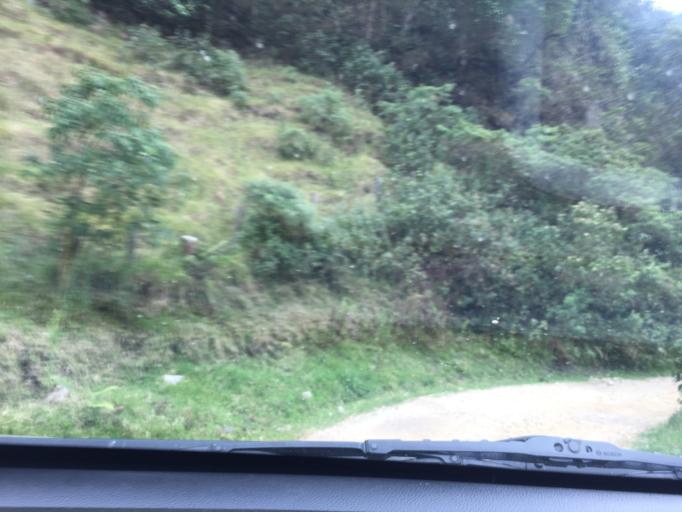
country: CO
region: Cundinamarca
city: Bojaca
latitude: 4.7000
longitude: -74.3663
